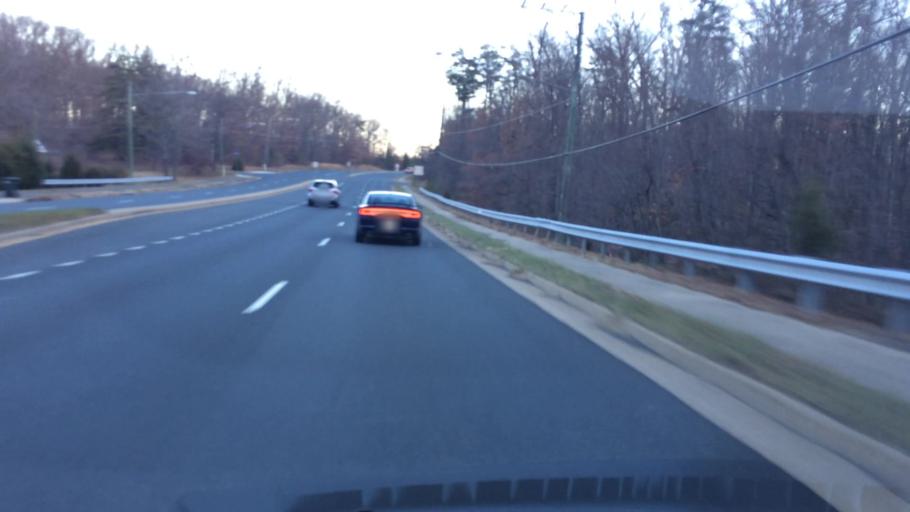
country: US
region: Virginia
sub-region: City of Fairfax
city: Fairfax
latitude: 38.8418
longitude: -77.3414
